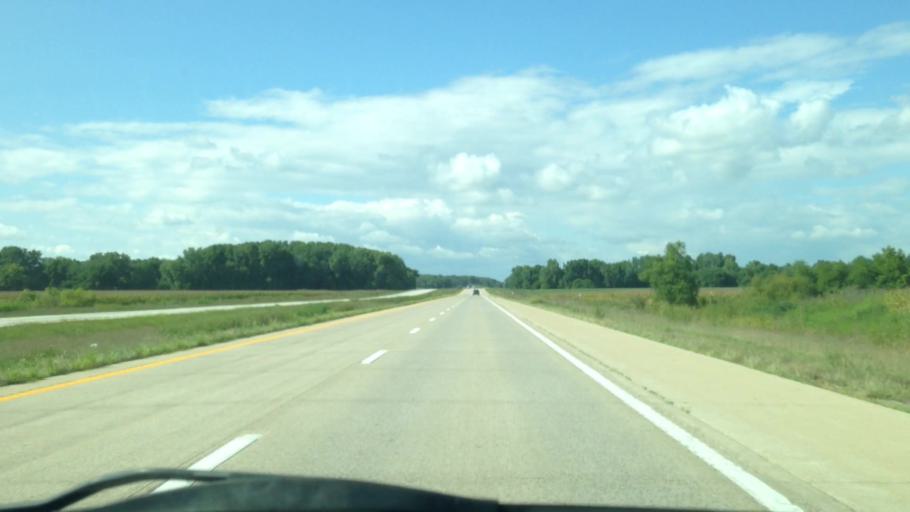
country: US
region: Illinois
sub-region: Hancock County
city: Warsaw
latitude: 40.2923
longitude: -91.5687
